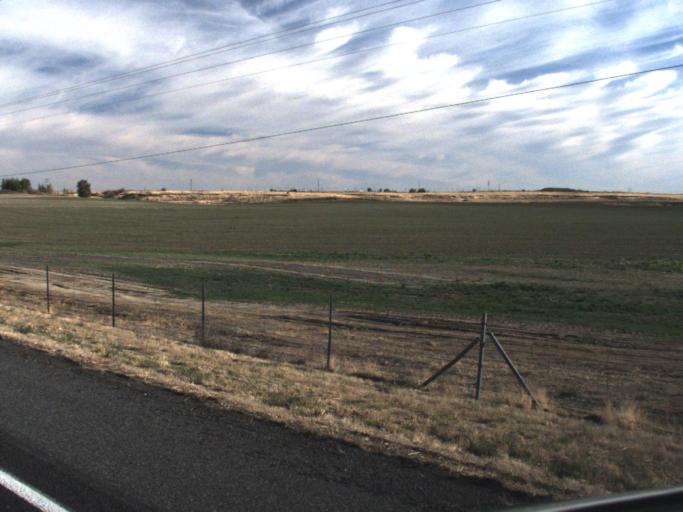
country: US
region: Washington
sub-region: Franklin County
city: Basin City
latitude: 46.6147
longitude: -119.0062
